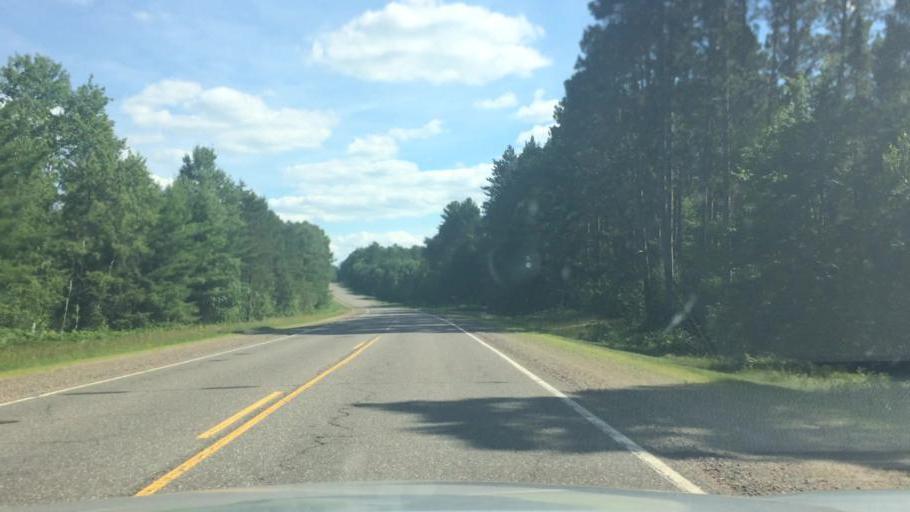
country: US
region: Wisconsin
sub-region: Vilas County
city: Lac du Flambeau
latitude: 46.0482
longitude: -89.6500
